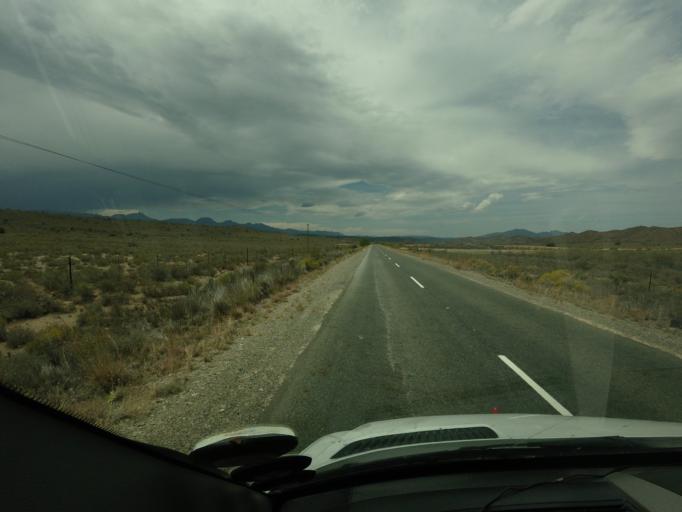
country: ZA
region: Western Cape
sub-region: Eden District Municipality
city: Ladismith
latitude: -33.6022
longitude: 21.0846
